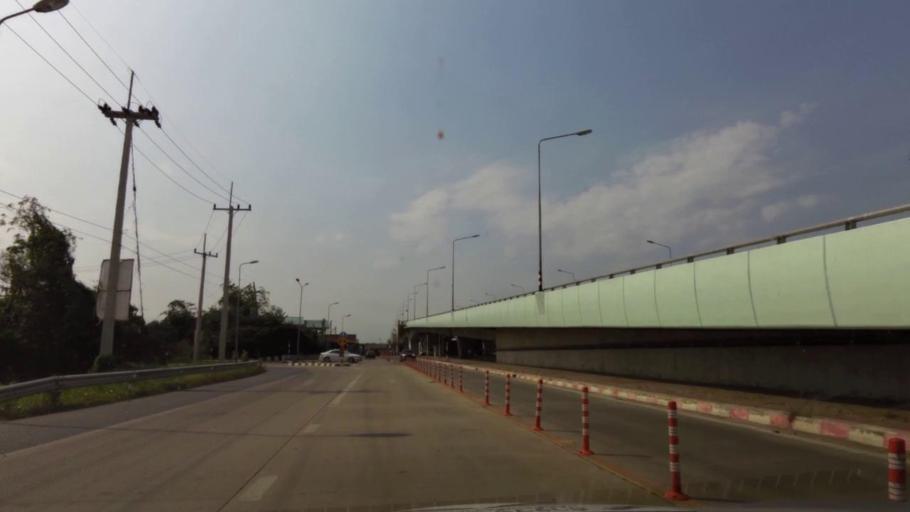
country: TH
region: Phra Nakhon Si Ayutthaya
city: Phra Nakhon Si Ayutthaya
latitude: 14.3280
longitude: 100.5822
